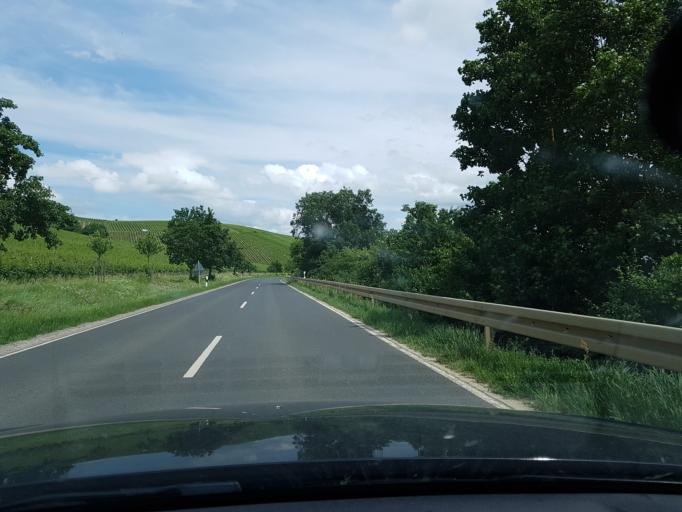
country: DE
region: Bavaria
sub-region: Regierungsbezirk Unterfranken
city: Nordheim
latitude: 49.8736
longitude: 10.1855
